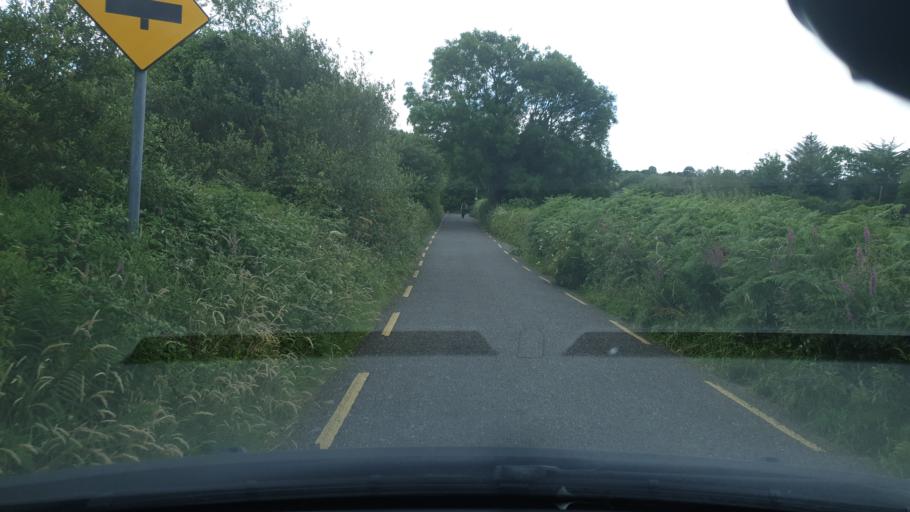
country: IE
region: Munster
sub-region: Ciarrai
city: Tralee
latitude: 52.2429
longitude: -9.6452
